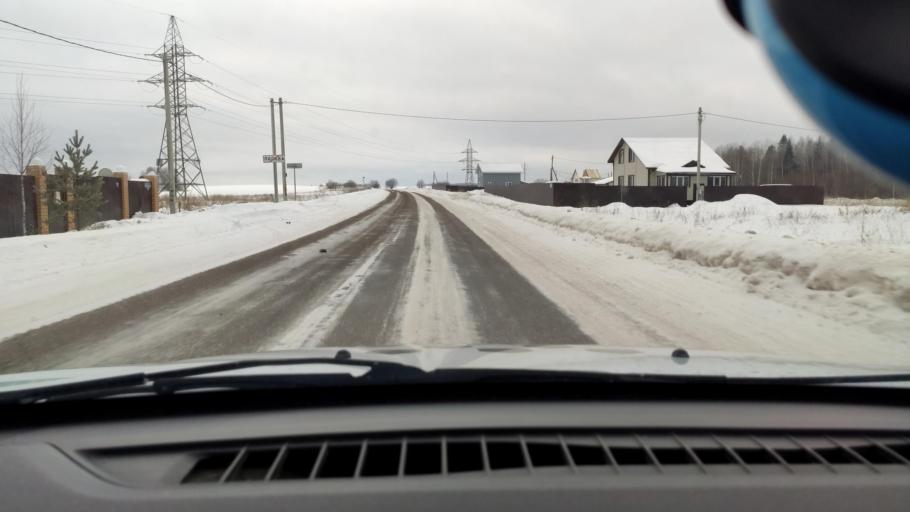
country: RU
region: Perm
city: Overyata
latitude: 58.0731
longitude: 55.9513
